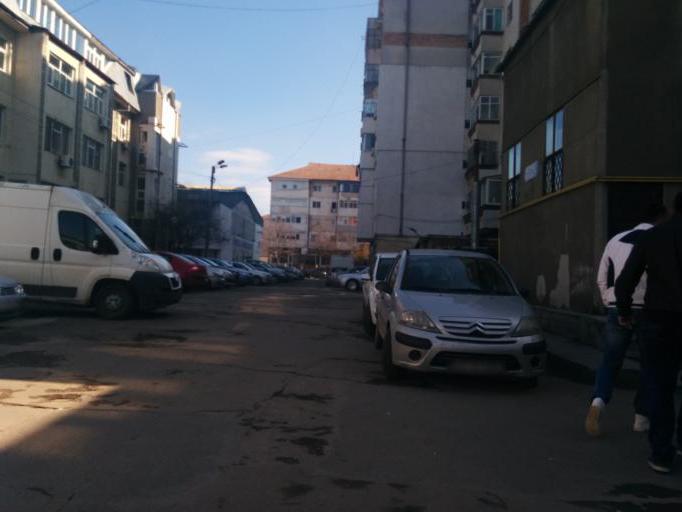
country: RO
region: Ialomita
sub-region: Comuna Slobozia
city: Slobozia
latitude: 44.5629
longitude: 27.3667
